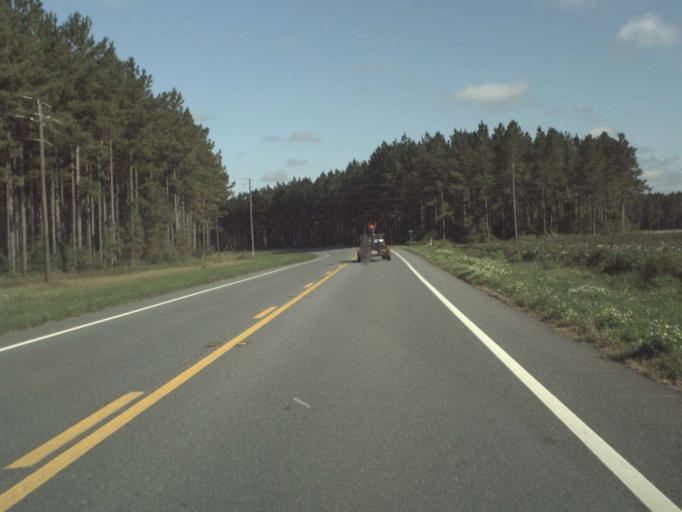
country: US
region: Florida
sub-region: Gulf County
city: Wewahitchka
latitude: 30.2255
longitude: -85.2046
